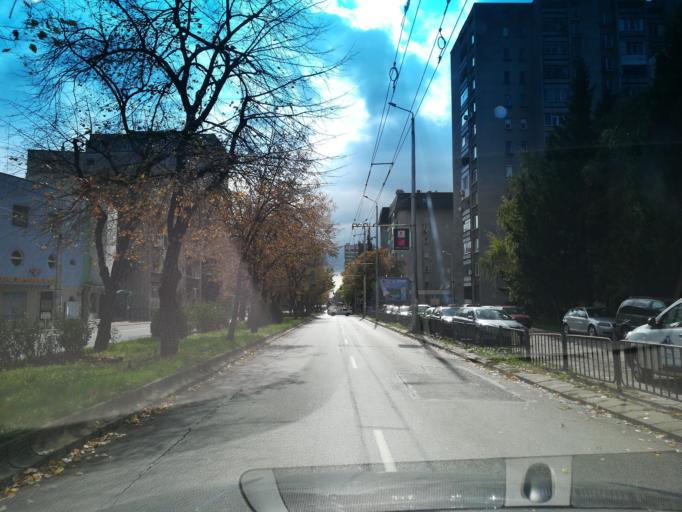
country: BG
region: Stara Zagora
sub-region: Obshtina Stara Zagora
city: Stara Zagora
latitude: 42.4314
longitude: 25.6327
